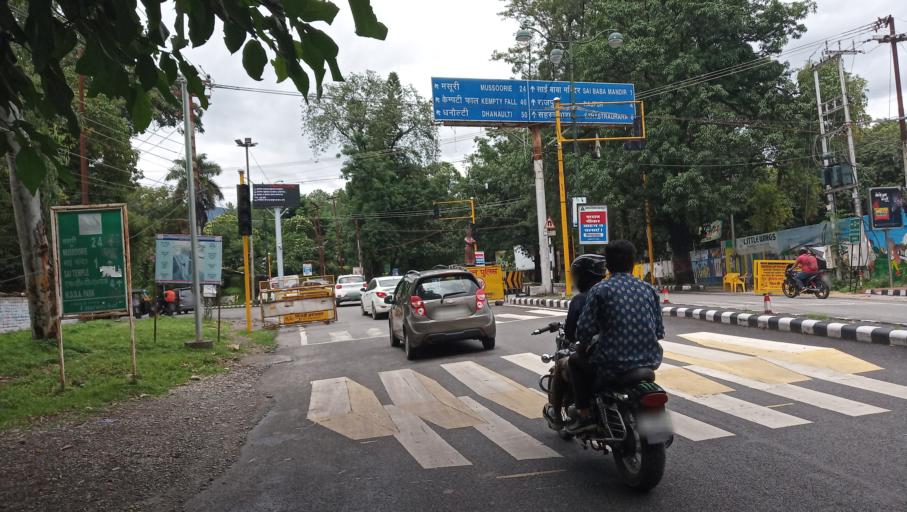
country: IN
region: Uttarakhand
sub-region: Dehradun
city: Raipur
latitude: 30.3712
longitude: 78.0771
